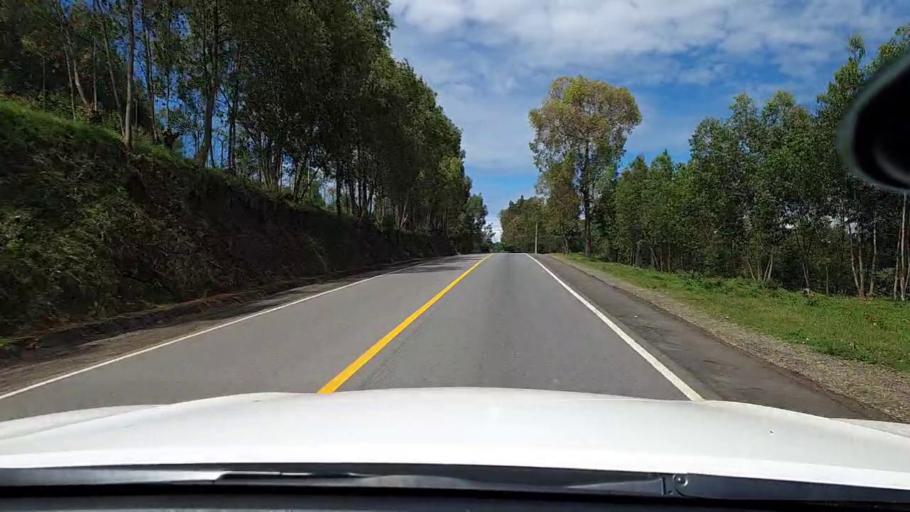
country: RW
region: Kigali
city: Kigali
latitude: -1.8239
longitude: 29.9456
